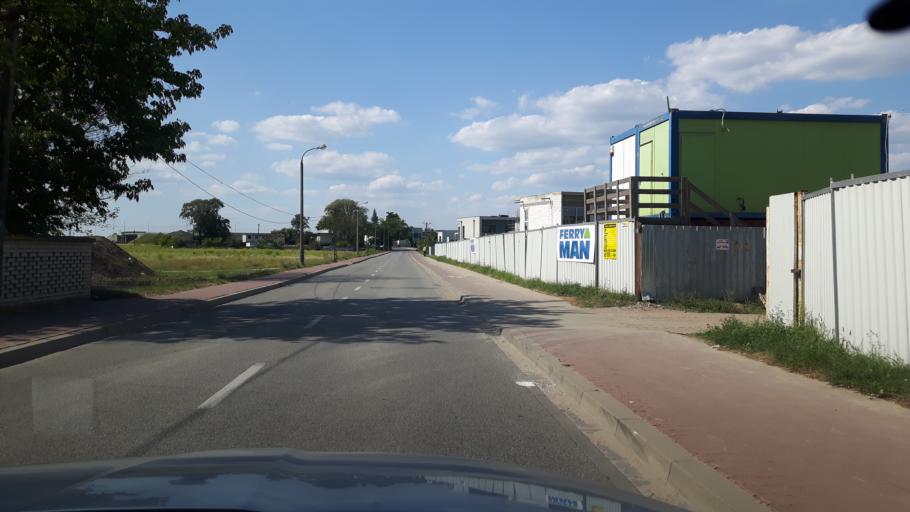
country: PL
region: Masovian Voivodeship
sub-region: Powiat pruszkowski
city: Nowe Grocholice
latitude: 52.1618
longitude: 20.9135
